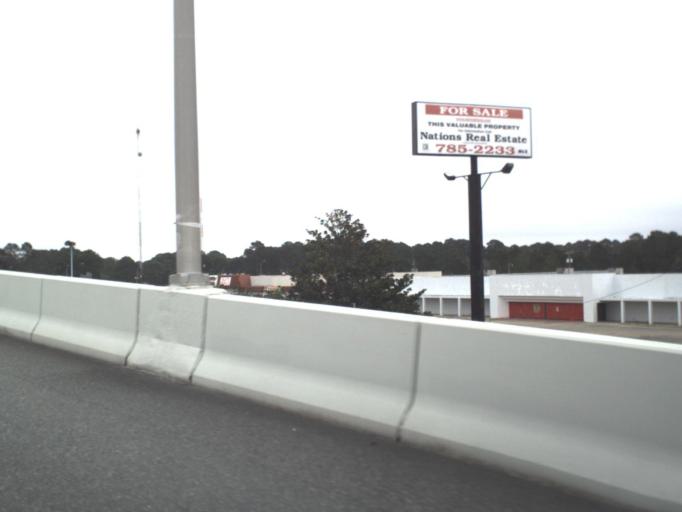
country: US
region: Florida
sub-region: Bay County
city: Upper Grand Lagoon
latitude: 30.1877
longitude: -85.7652
